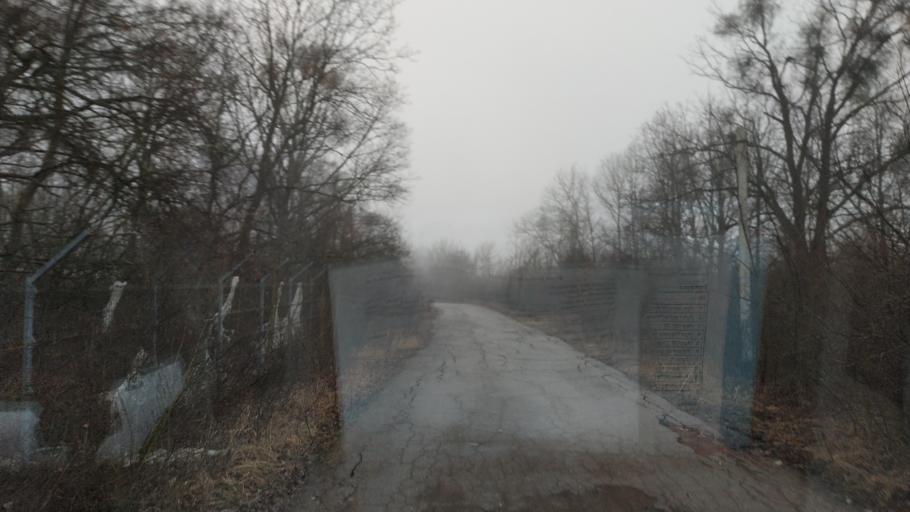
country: MD
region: Laloveni
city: Ialoveni
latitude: 46.9492
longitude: 28.6998
